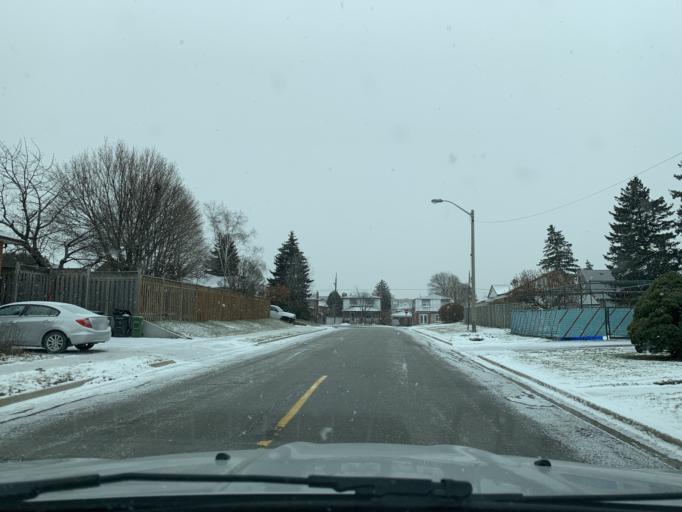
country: CA
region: Ontario
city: Concord
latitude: 43.7335
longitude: -79.4873
